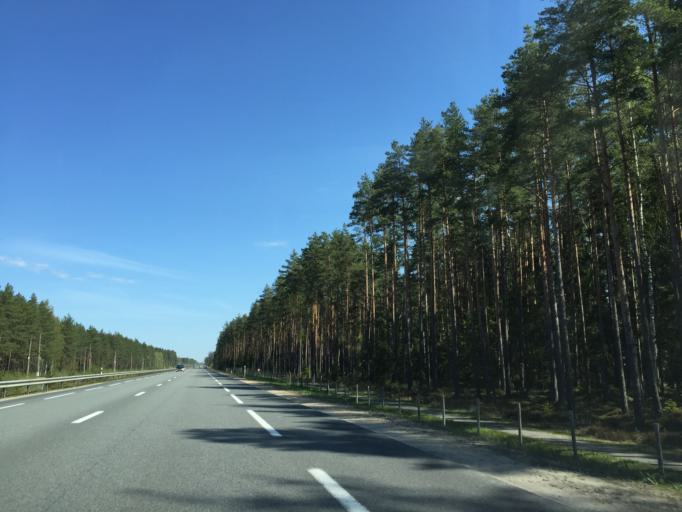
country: LV
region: Saulkrastu
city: Saulkrasti
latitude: 57.2912
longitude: 24.4359
